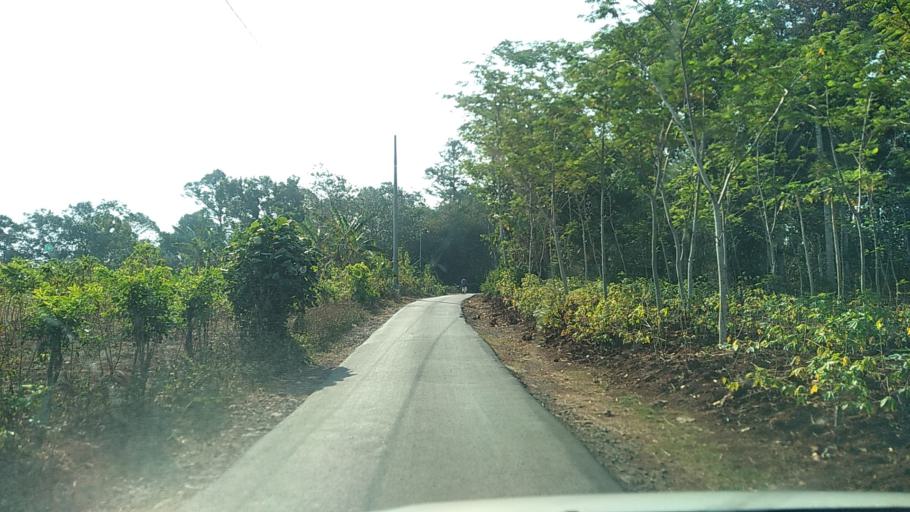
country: ID
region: Central Java
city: Semarang
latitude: -7.0196
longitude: 110.3172
